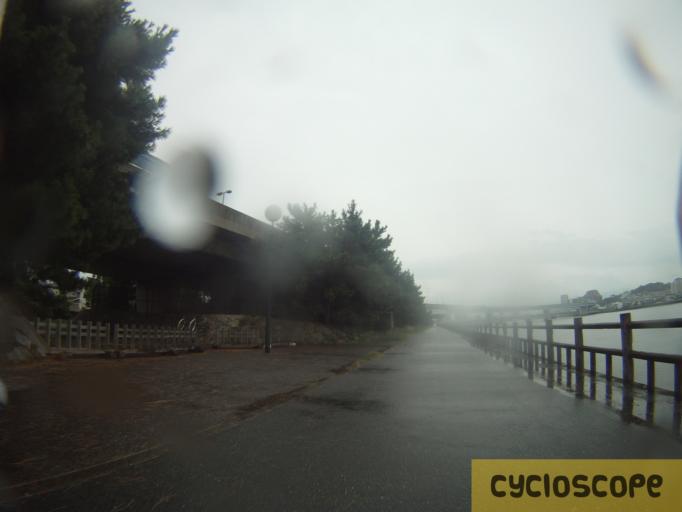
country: JP
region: Fukuoka
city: Fukuoka-shi
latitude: 33.5883
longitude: 130.3447
